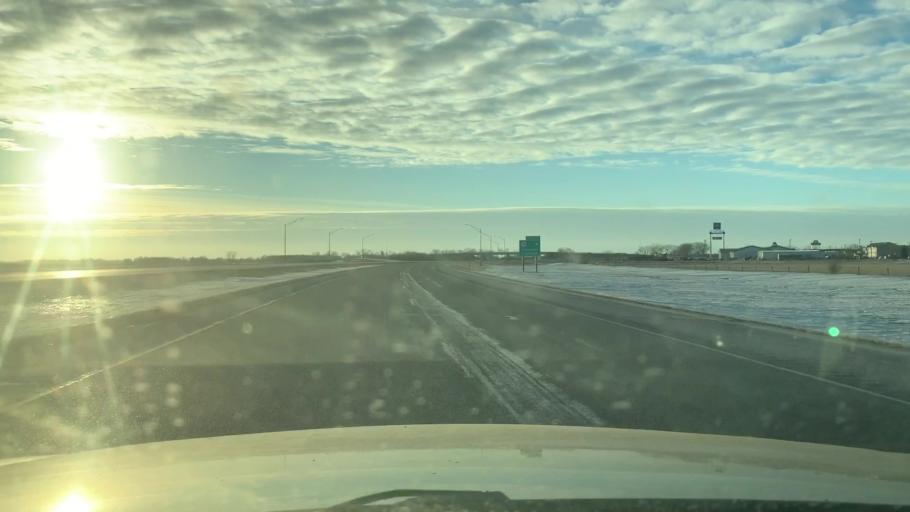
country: US
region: North Dakota
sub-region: Cass County
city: Casselton
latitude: 46.8749
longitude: -97.2023
